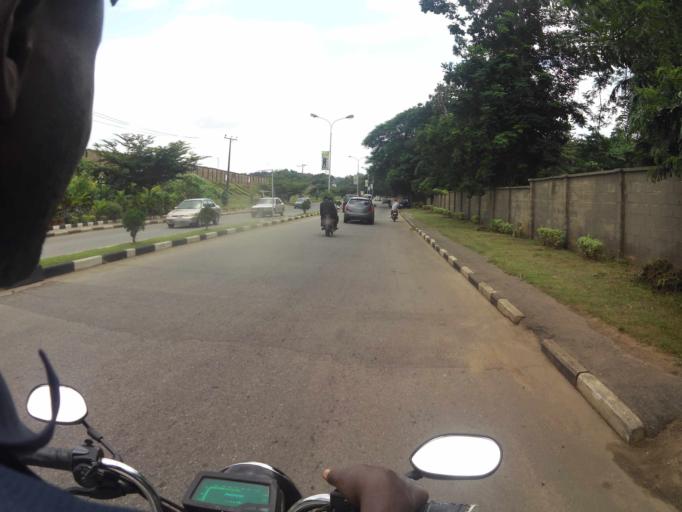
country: NG
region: Oyo
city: Ibadan
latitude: 7.4065
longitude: 3.9031
